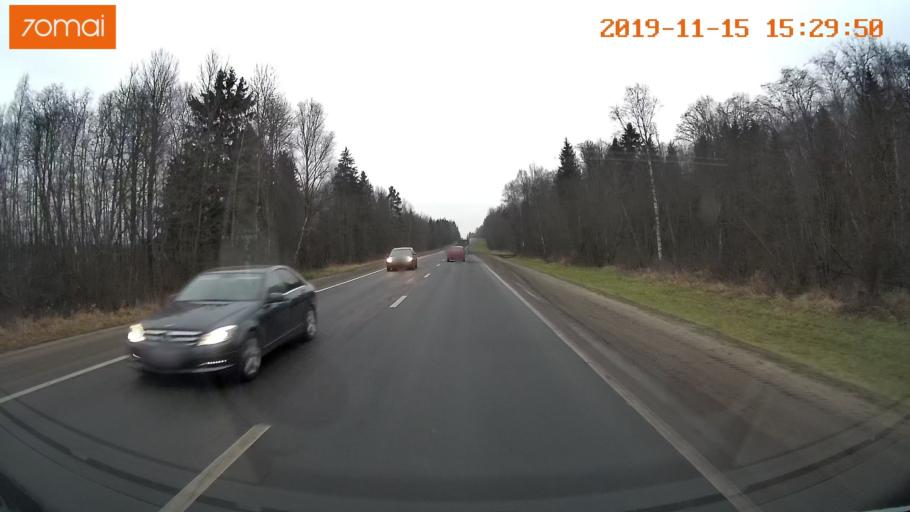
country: RU
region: Jaroslavl
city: Danilov
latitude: 58.1162
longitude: 40.1168
